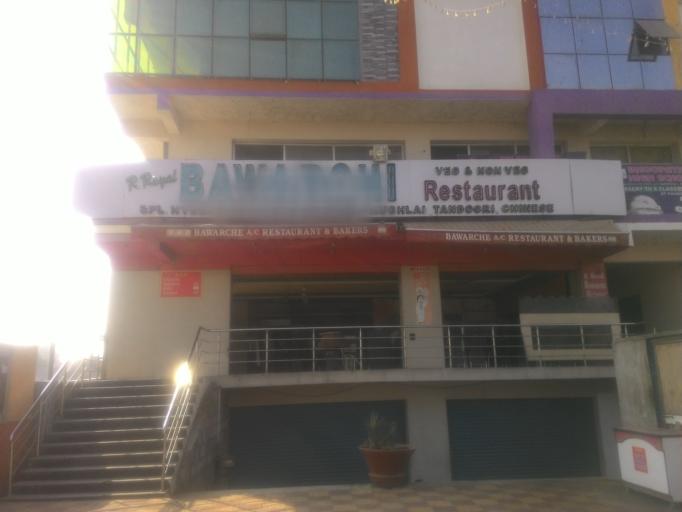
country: IN
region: Telangana
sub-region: Rangareddi
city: Ghatkesar
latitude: 17.4177
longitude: 78.6313
